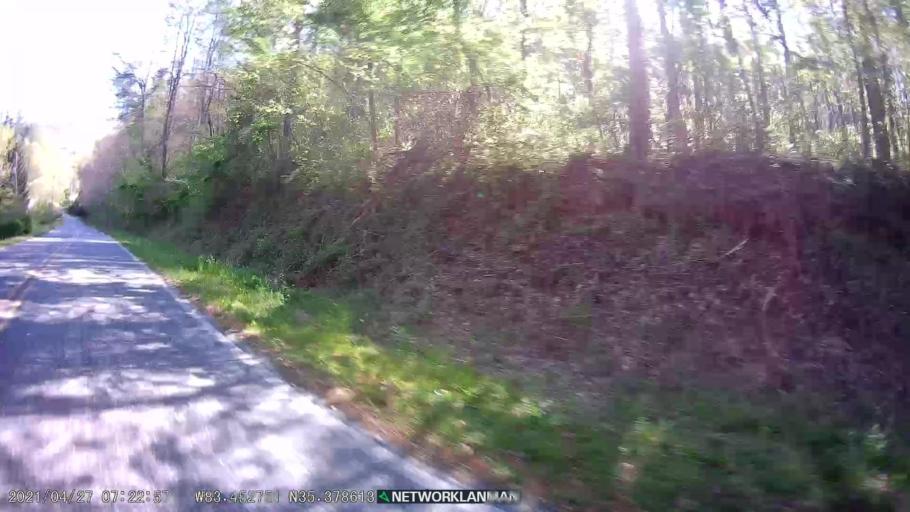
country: US
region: North Carolina
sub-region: Swain County
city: Bryson City
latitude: 35.3787
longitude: -83.4528
